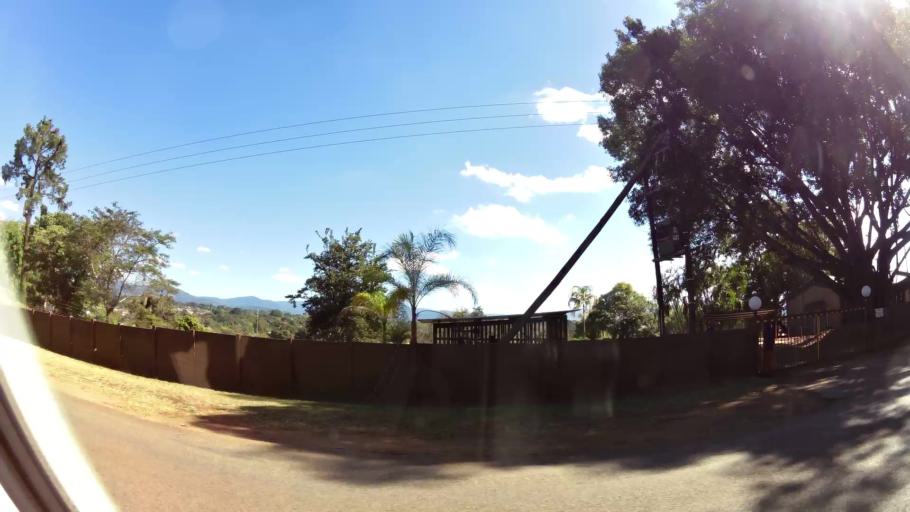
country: ZA
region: Limpopo
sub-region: Mopani District Municipality
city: Tzaneen
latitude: -23.8198
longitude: 30.1696
